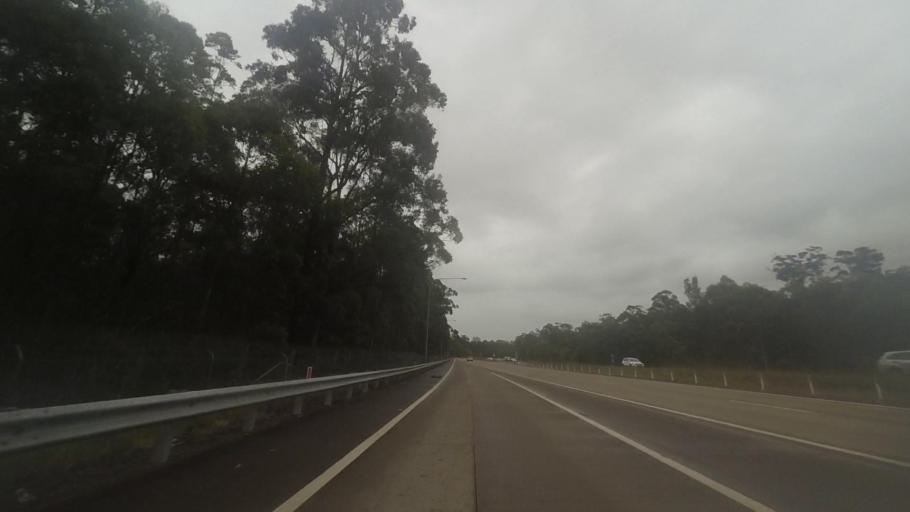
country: AU
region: New South Wales
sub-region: Port Stephens Shire
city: Medowie
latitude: -32.6490
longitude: 151.9123
